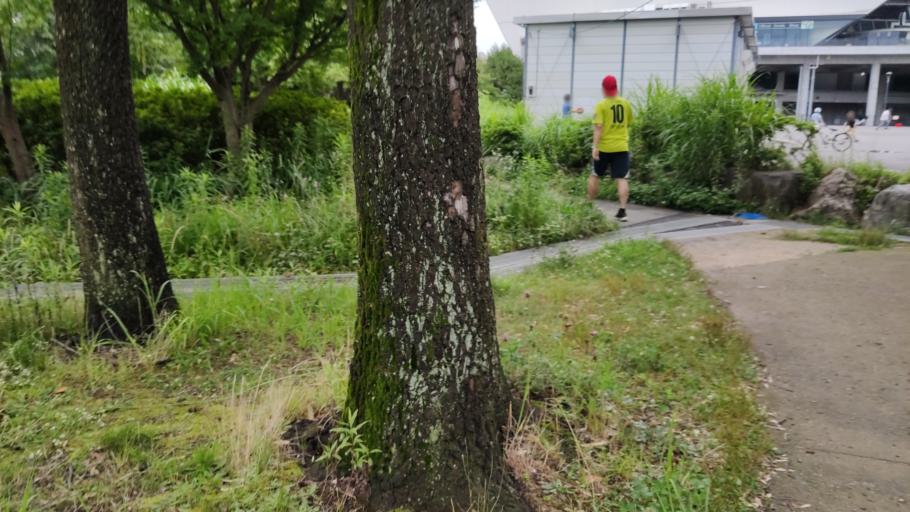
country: JP
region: Kanagawa
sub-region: Kawasaki-shi
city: Kawasaki
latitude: 35.5869
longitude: 139.6507
